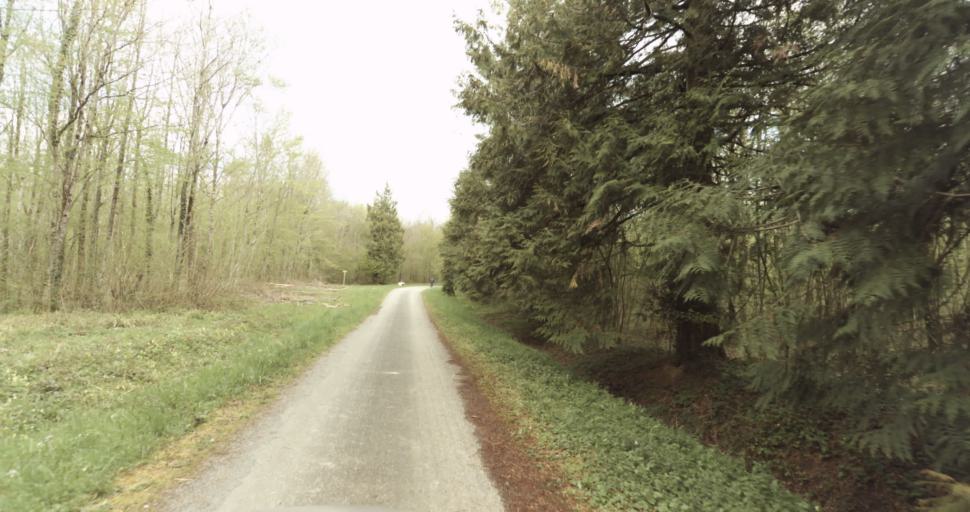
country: FR
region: Bourgogne
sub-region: Departement de la Cote-d'Or
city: Auxonne
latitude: 47.1670
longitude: 5.4235
